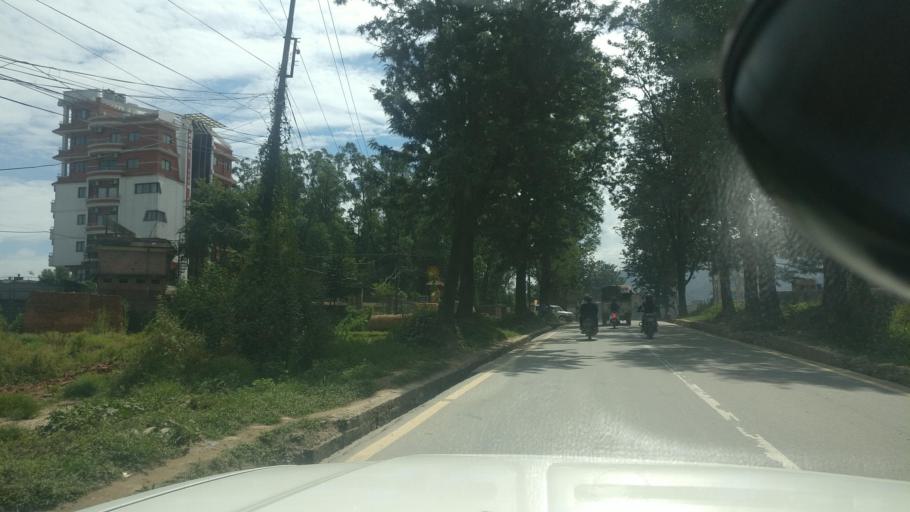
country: NP
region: Central Region
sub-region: Bagmati Zone
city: Bhaktapur
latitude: 27.6631
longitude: 85.4438
